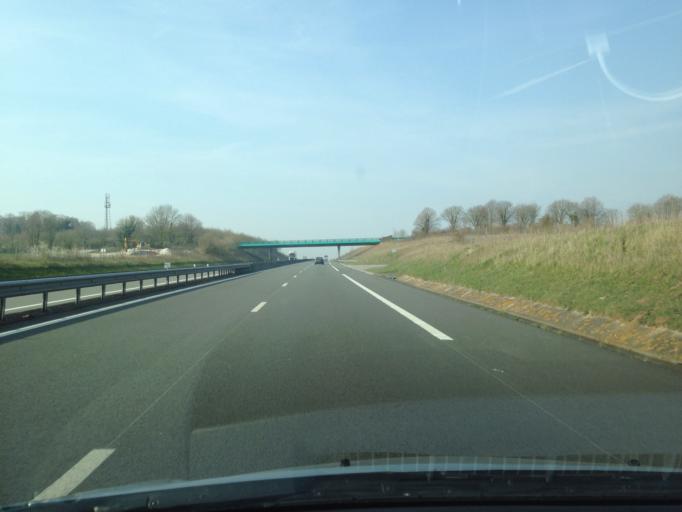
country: FR
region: Picardie
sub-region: Departement de la Somme
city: Rue
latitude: 50.2765
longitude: 1.7341
